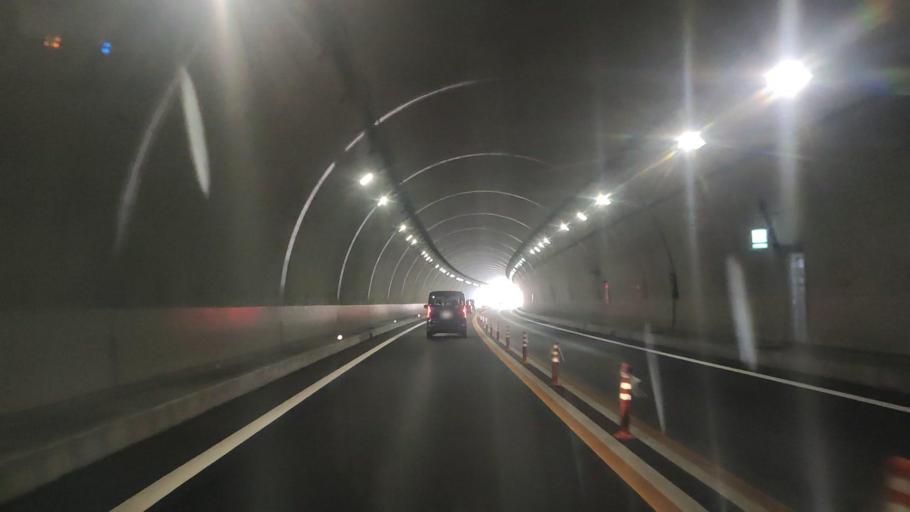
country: JP
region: Fukuoka
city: Nakatsu
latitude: 33.5199
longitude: 131.2572
